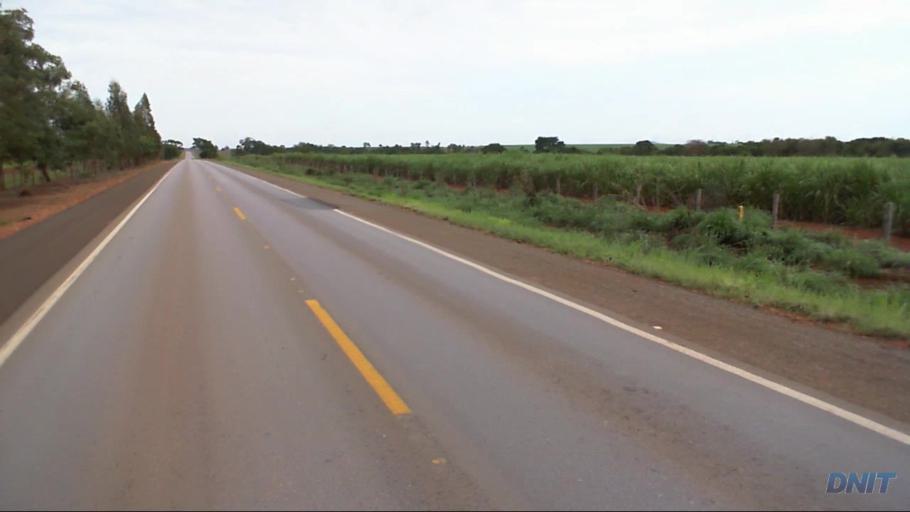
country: BR
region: Goias
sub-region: Uruacu
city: Uruacu
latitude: -14.7145
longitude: -49.1059
